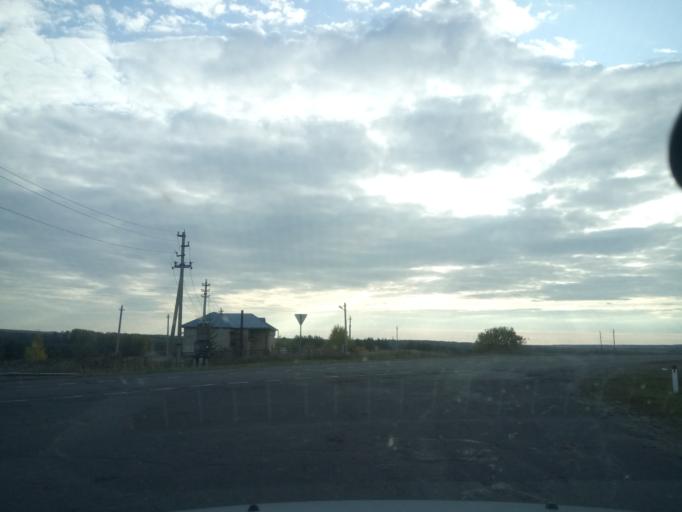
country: RU
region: Nizjnij Novgorod
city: Bol'shoye Boldino
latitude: 54.9913
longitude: 45.3065
